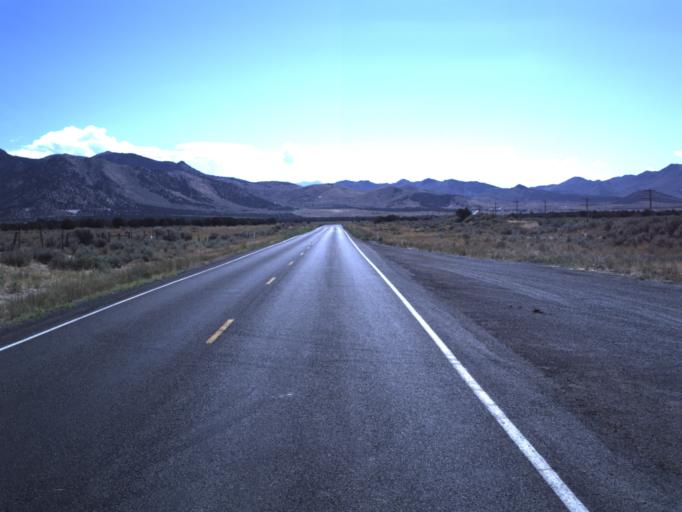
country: US
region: Utah
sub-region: Utah County
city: Genola
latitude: 39.9428
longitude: -112.1949
